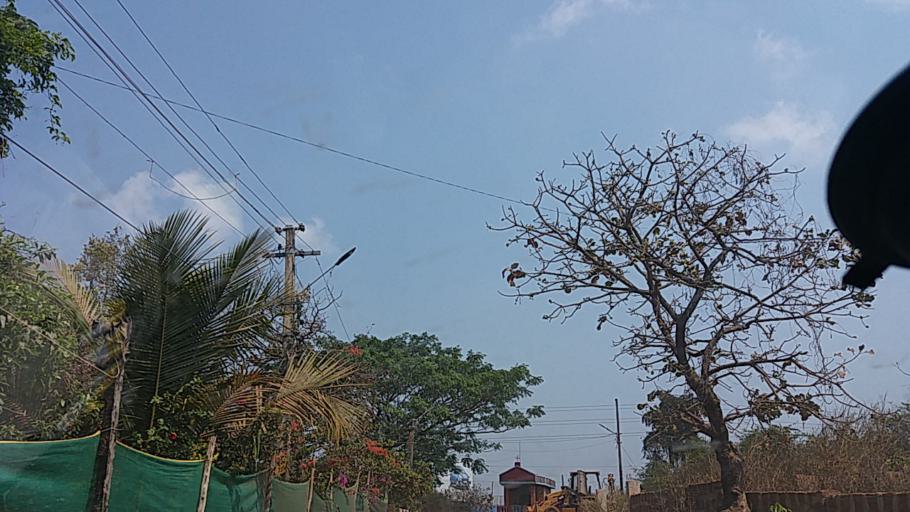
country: IN
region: Goa
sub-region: South Goa
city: Sancoale
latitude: 15.3768
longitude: 73.9125
